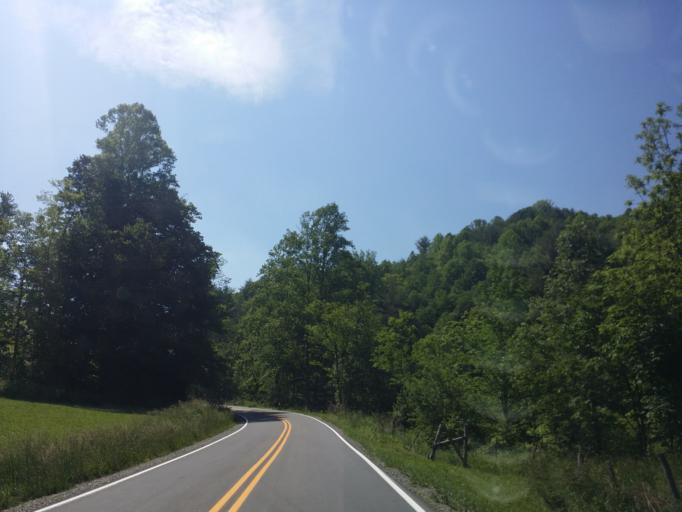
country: US
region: North Carolina
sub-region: Madison County
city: Marshall
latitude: 35.7466
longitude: -82.8604
